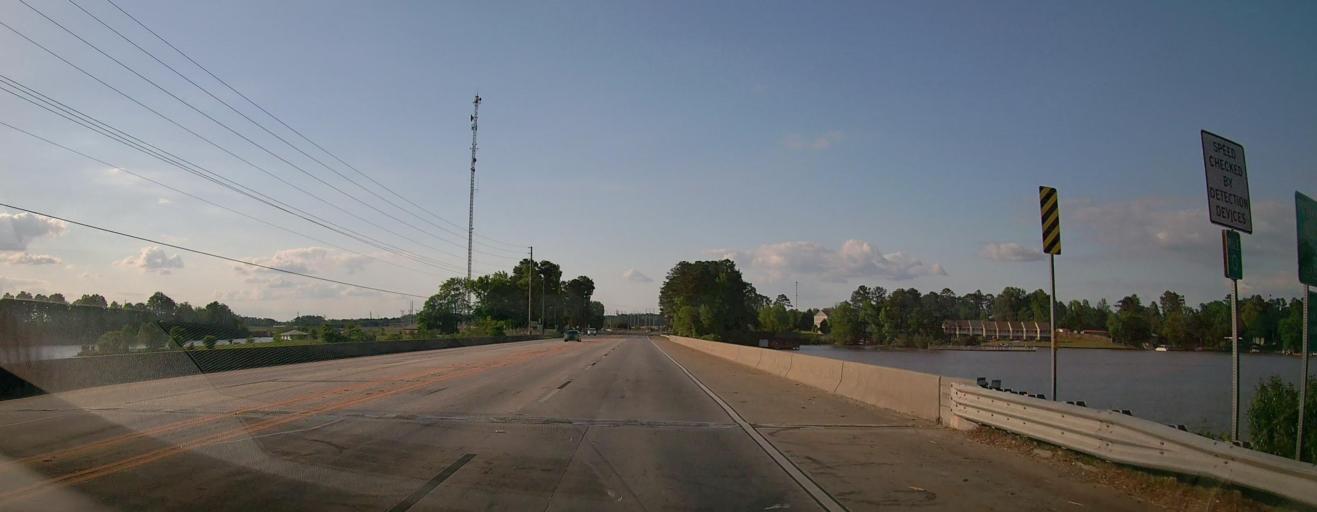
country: US
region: Georgia
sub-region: Baldwin County
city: Milledgeville
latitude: 33.1894
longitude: -83.2927
